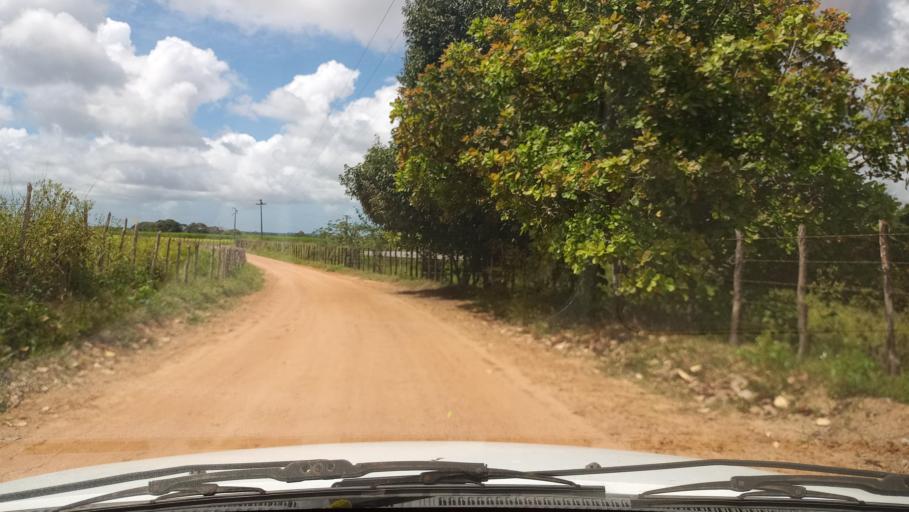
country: BR
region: Rio Grande do Norte
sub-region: Goianinha
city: Goianinha
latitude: -6.2604
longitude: -35.2470
